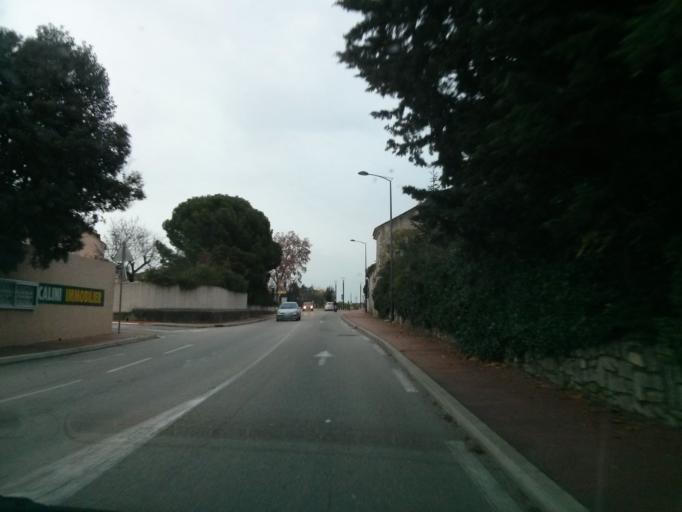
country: FR
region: Languedoc-Roussillon
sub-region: Departement du Gard
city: Caveirac
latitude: 43.8224
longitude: 4.2655
